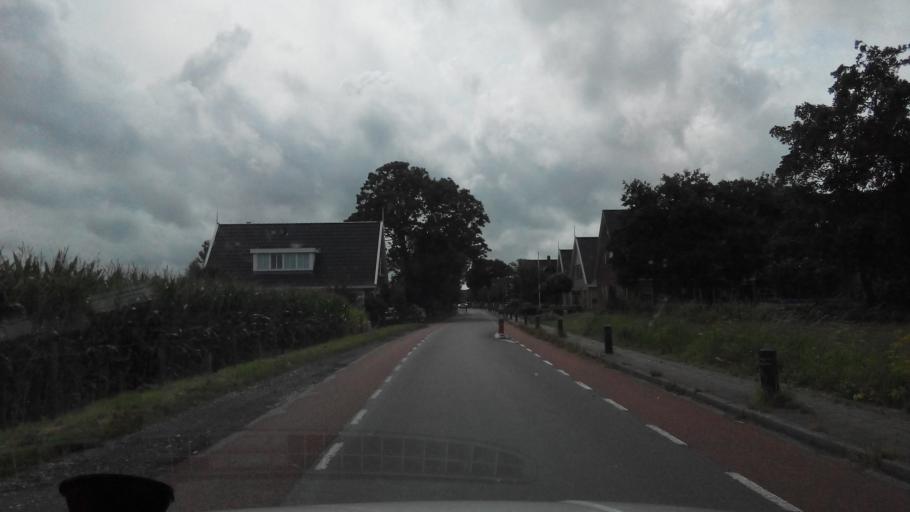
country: NL
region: North Holland
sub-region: Gemeente Hollands Kroon
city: Den Oever
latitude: 52.8968
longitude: 4.9374
